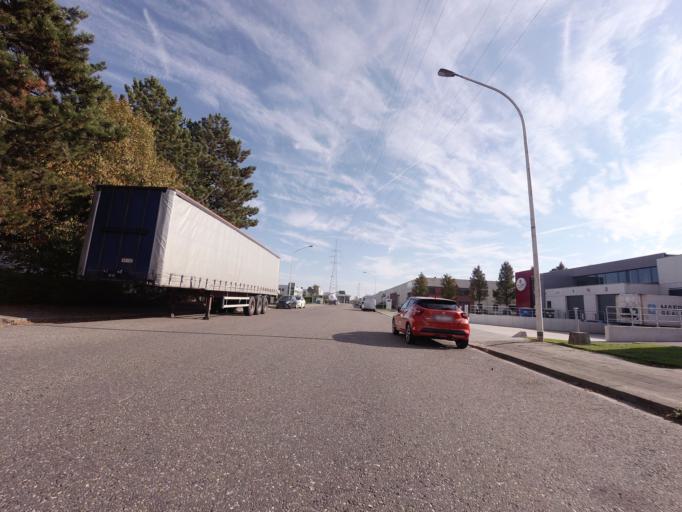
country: BE
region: Flanders
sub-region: Provincie Antwerpen
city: Schoten
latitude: 51.2334
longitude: 4.4968
